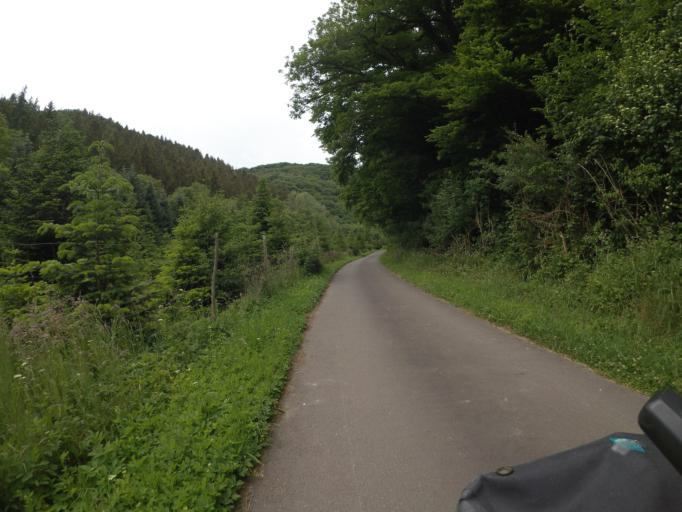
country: DE
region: Rheinland-Pfalz
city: Merschbach
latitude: 49.7897
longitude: 7.0036
